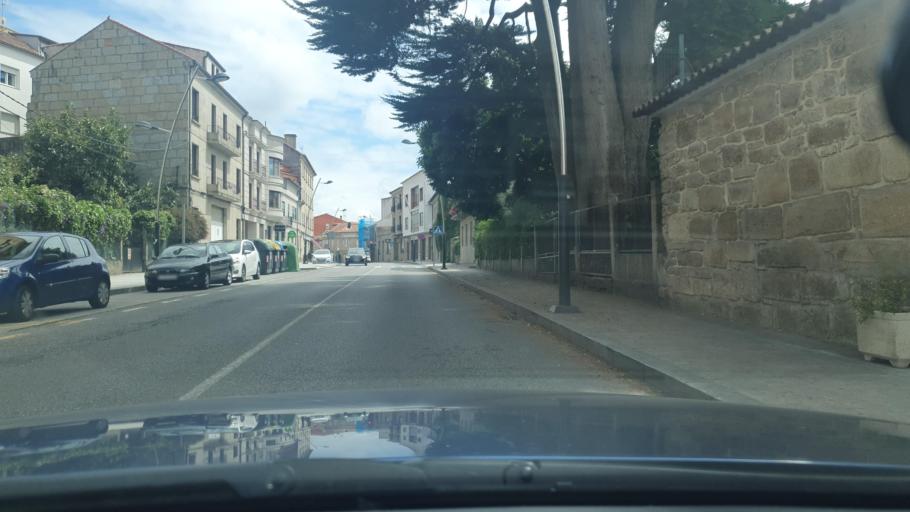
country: ES
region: Galicia
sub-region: Provincia de Pontevedra
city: Cambados
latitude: 42.5120
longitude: -8.8159
